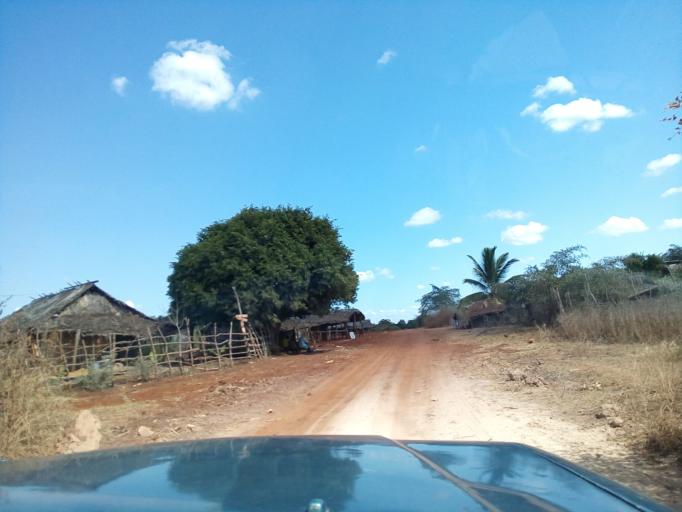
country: MG
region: Boeny
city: Mahajanga
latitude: -15.9989
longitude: 46.0534
